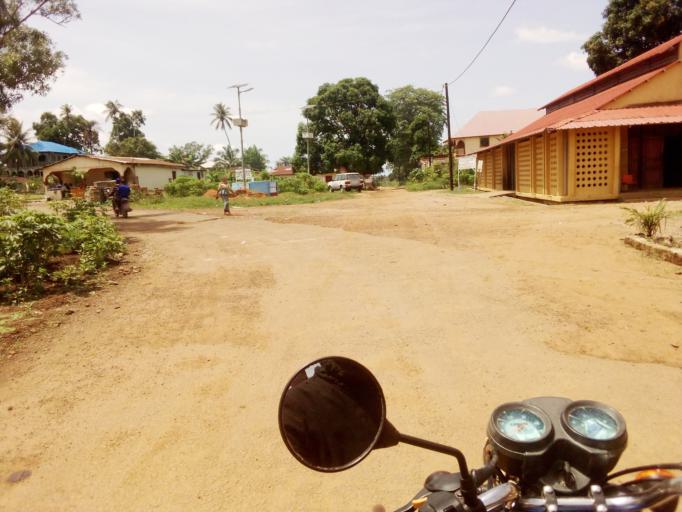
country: SL
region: Western Area
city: Waterloo
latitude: 8.3394
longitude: -13.0679
